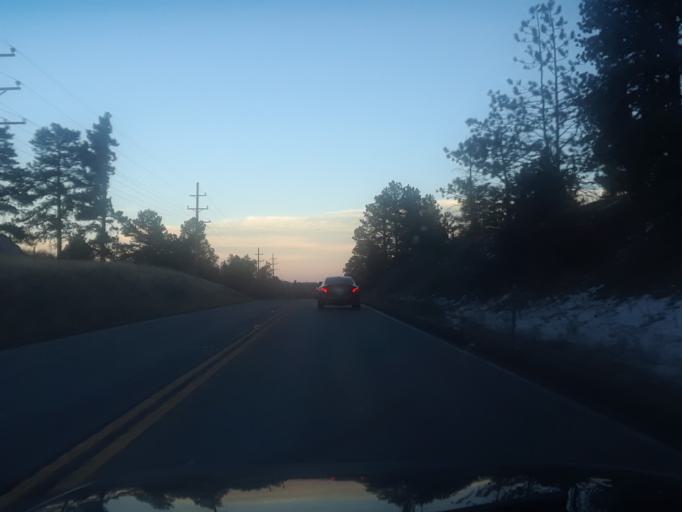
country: US
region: Colorado
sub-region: Clear Creek County
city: Georgetown
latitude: 39.4284
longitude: -105.5696
